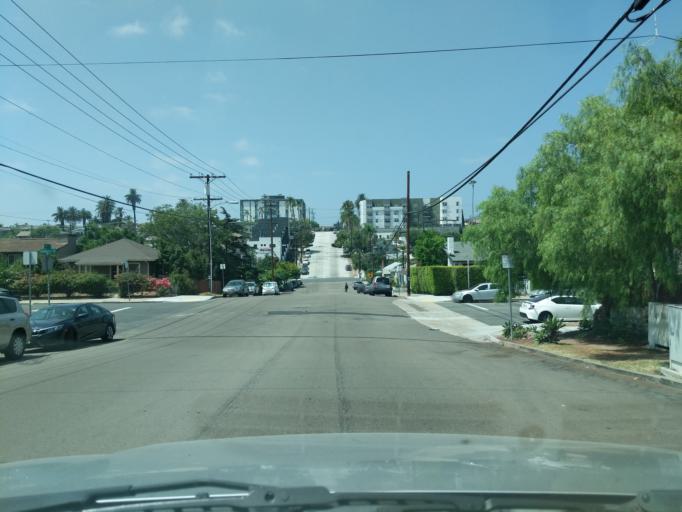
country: US
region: California
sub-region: San Diego County
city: San Diego
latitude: 32.7522
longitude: -117.1422
